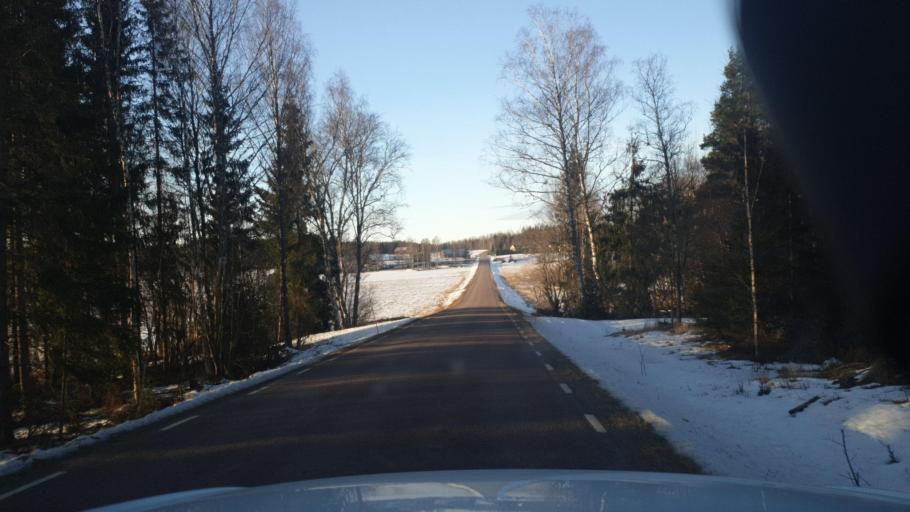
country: SE
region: Vaermland
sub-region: Karlstads Kommun
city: Edsvalla
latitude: 59.4927
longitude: 13.1003
